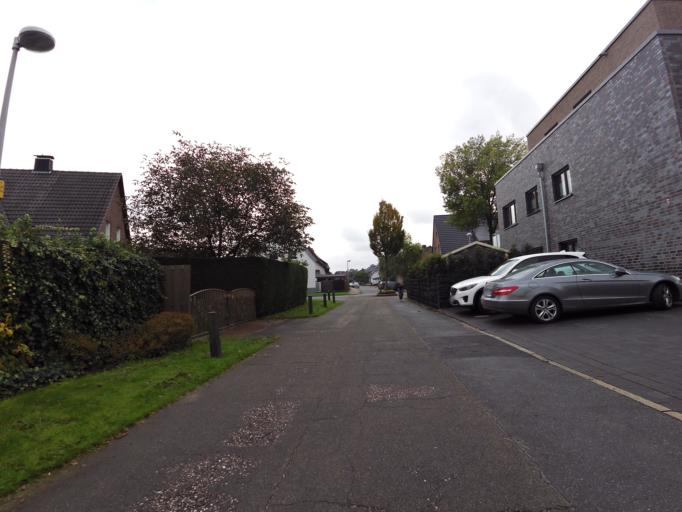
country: DE
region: North Rhine-Westphalia
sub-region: Regierungsbezirk Dusseldorf
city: Bocholt
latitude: 51.8330
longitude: 6.6022
